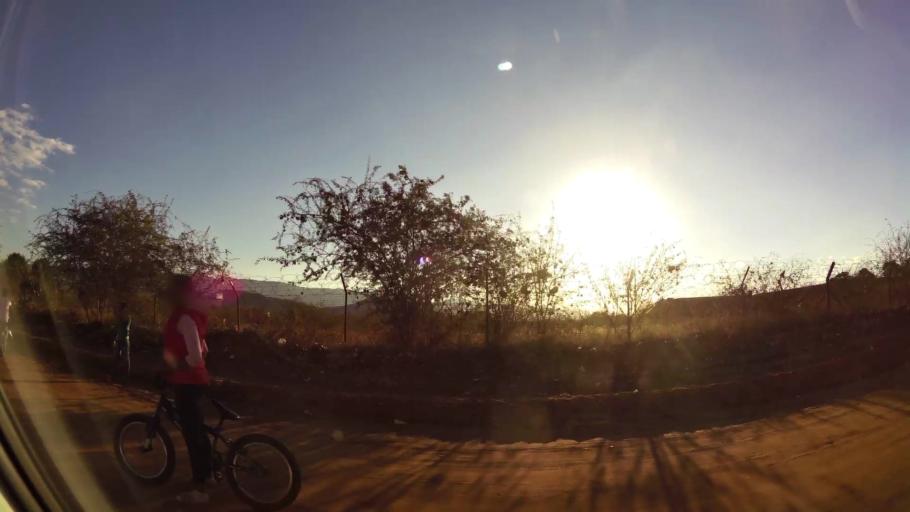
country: ZA
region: Limpopo
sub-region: Waterberg District Municipality
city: Mokopane
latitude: -24.1508
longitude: 28.9944
